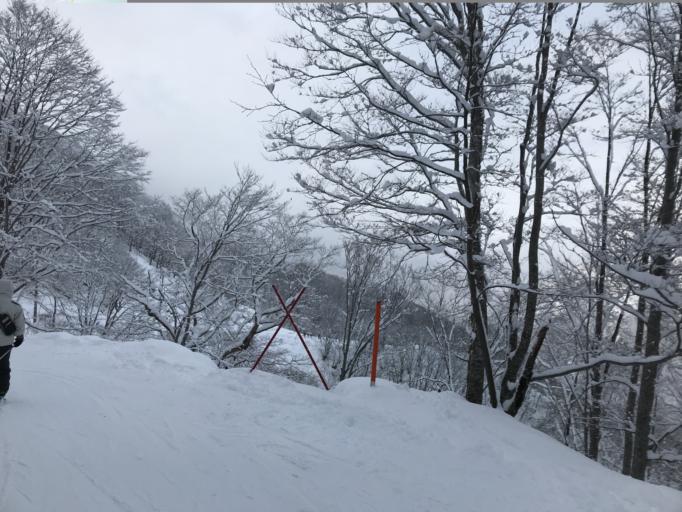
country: JP
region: Nagano
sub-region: Kitaazumi Gun
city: Hakuba
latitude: 36.7087
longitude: 137.8232
